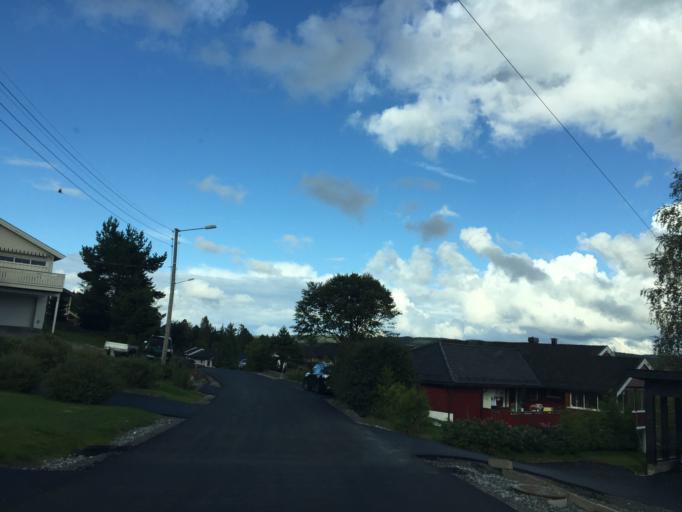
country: NO
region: Hedmark
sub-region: Kongsvinger
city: Kongsvinger
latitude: 60.1958
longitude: 12.0165
